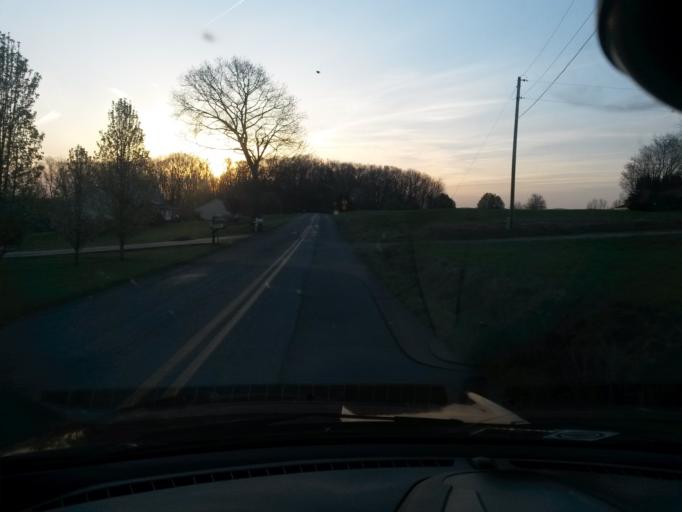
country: US
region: Virginia
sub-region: Botetourt County
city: Fincastle
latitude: 37.4750
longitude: -79.8511
